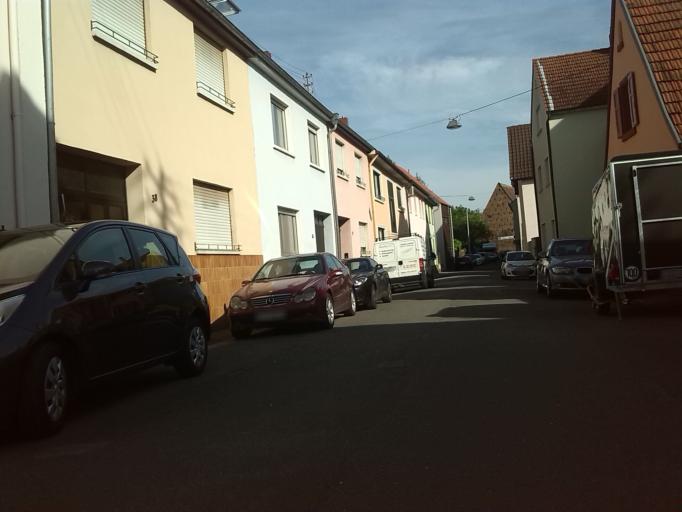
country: DE
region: Baden-Wuerttemberg
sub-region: Karlsruhe Region
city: Ilvesheim
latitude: 49.4704
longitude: 8.5613
